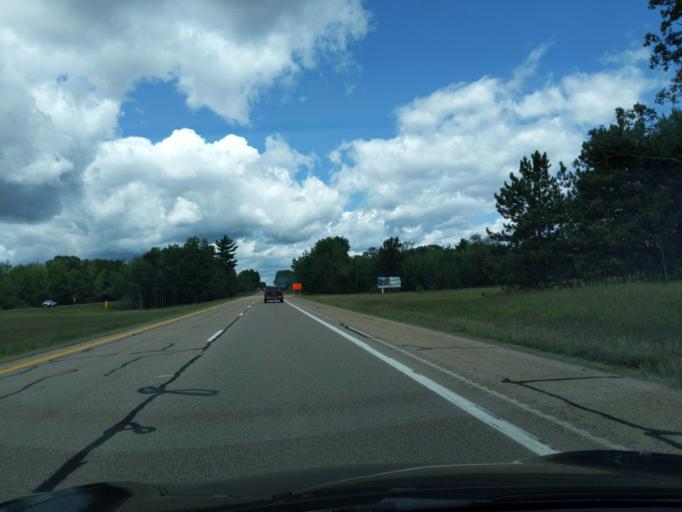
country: US
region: Michigan
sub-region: Roscommon County
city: Houghton Lake
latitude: 44.3154
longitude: -84.8058
